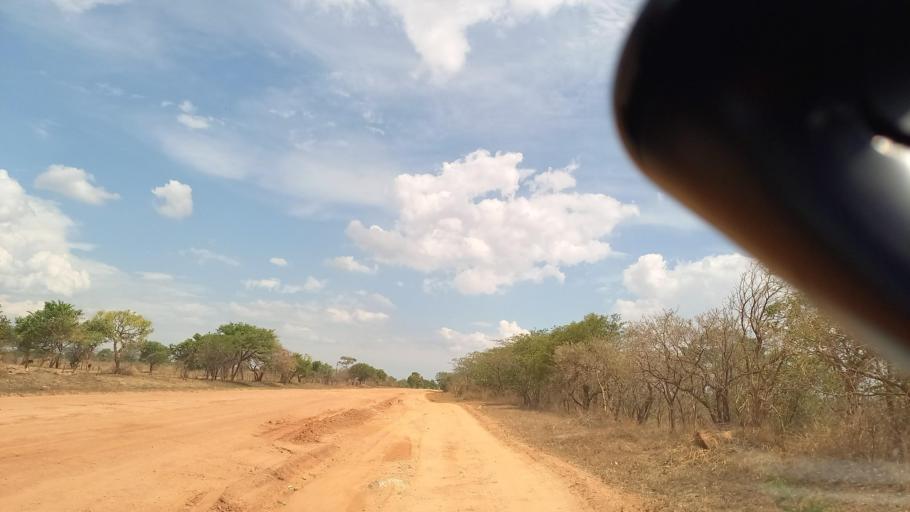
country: ZM
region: Lusaka
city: Kafue
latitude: -16.1184
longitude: 28.0365
